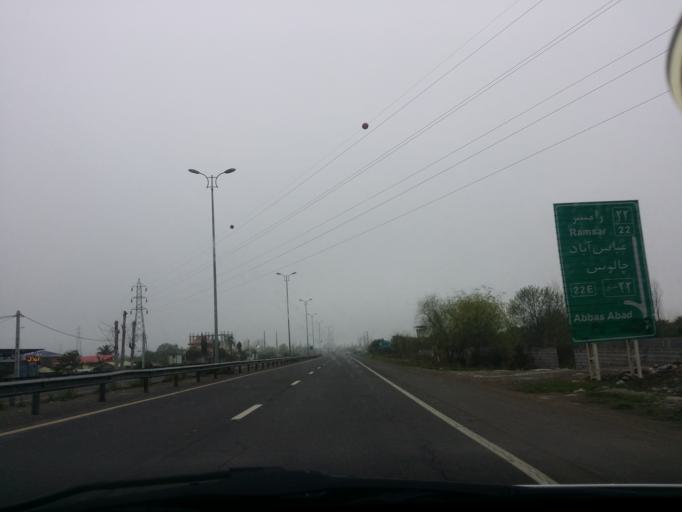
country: IR
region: Mazandaran
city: Tonekabon
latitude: 36.8273
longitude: 50.8440
